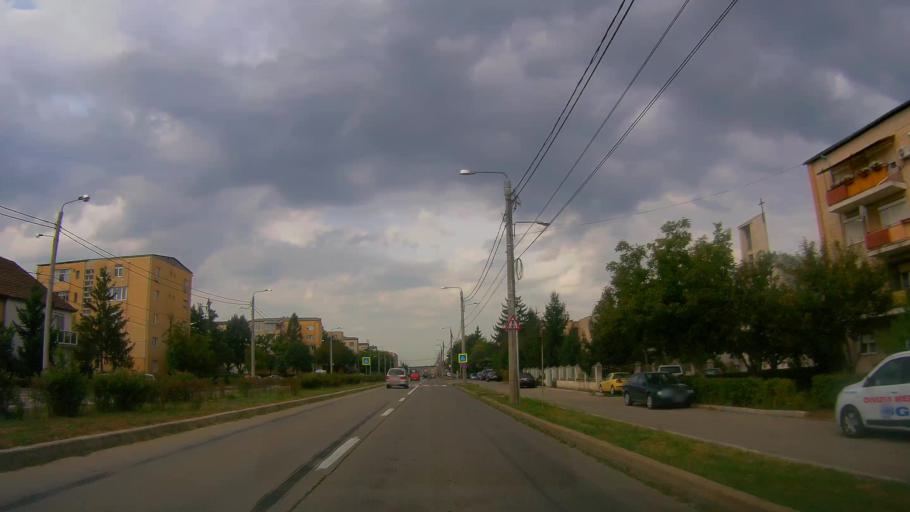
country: RO
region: Satu Mare
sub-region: Comuna Paulesti
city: Paulesti
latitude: 47.8019
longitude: 22.9057
